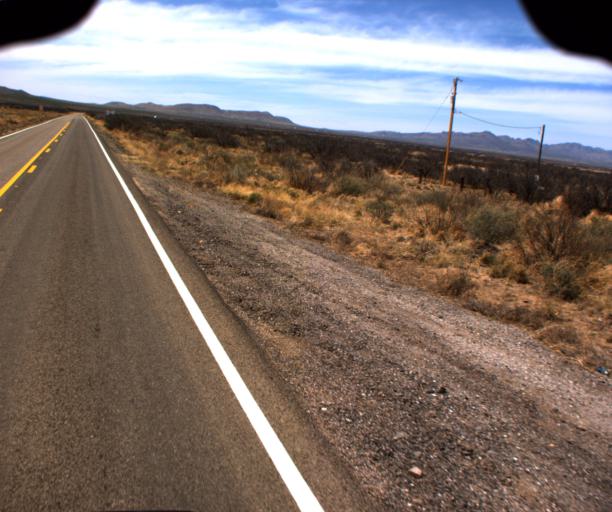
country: US
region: Arizona
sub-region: Cochise County
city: Willcox
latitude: 32.1391
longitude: -109.9186
